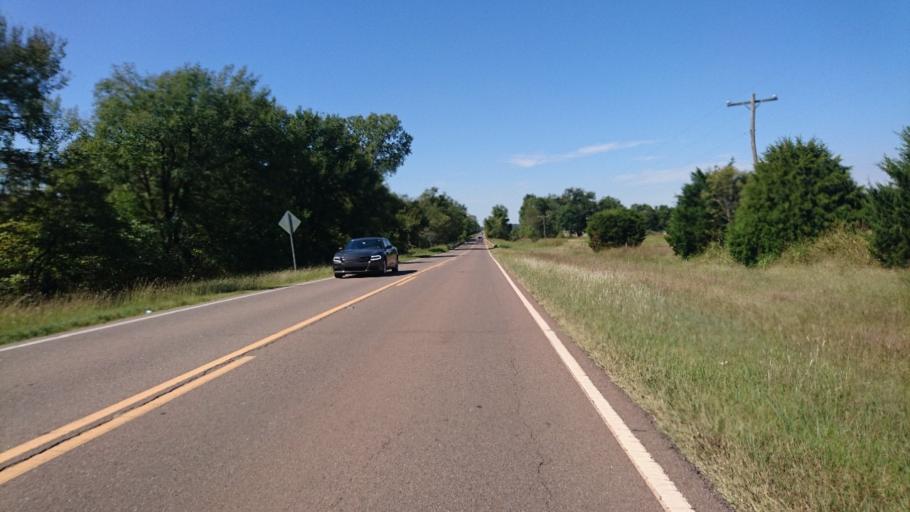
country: US
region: Oklahoma
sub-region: Oklahoma County
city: Luther
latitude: 35.6626
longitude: -97.2515
